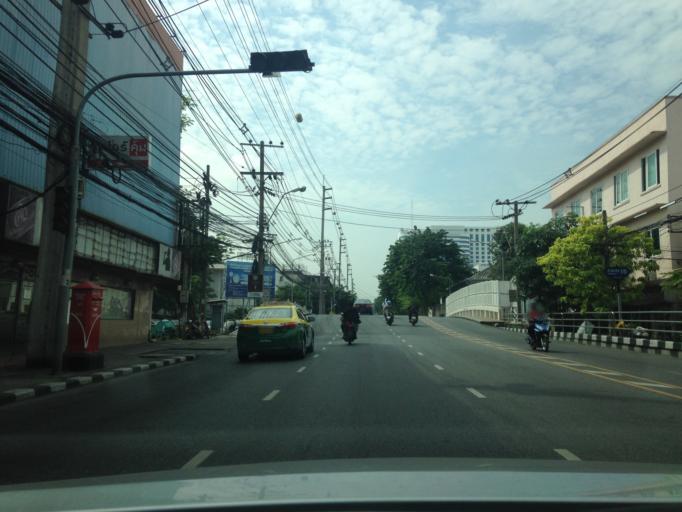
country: TH
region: Bangkok
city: Dusit
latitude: 13.7837
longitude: 100.5110
